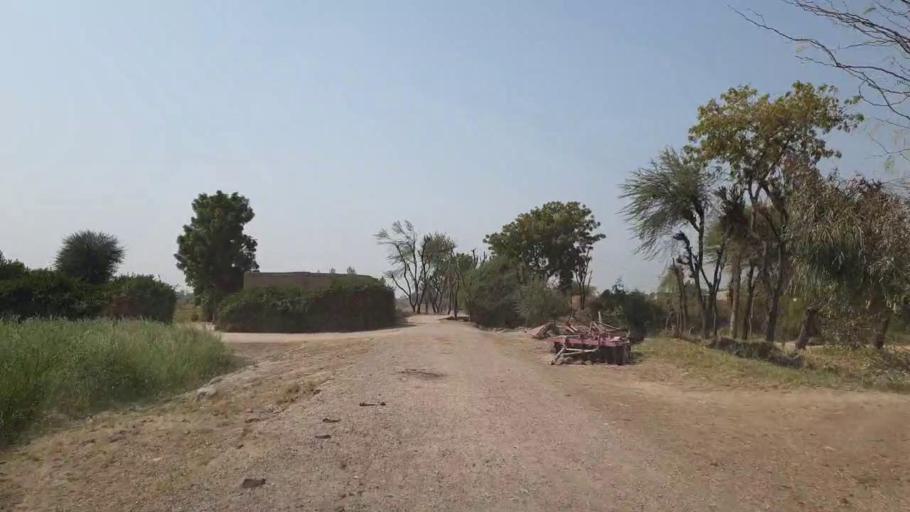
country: PK
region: Sindh
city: Mirpur Khas
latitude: 25.6459
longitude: 69.1269
